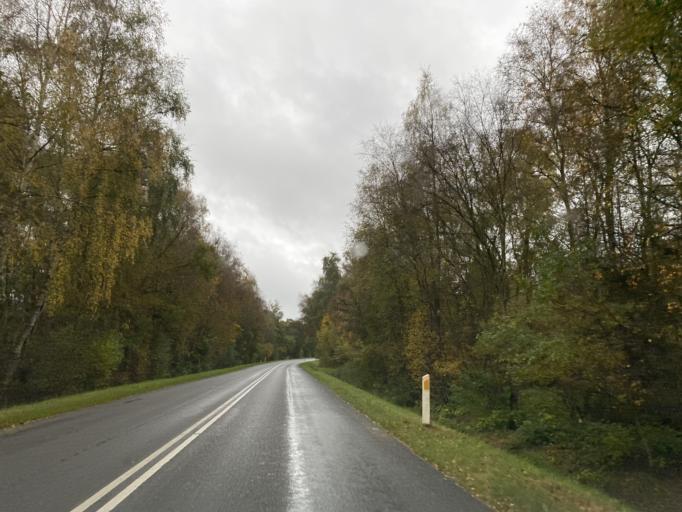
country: DK
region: Central Jutland
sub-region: Skanderborg Kommune
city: Ry
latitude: 56.1033
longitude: 9.7375
